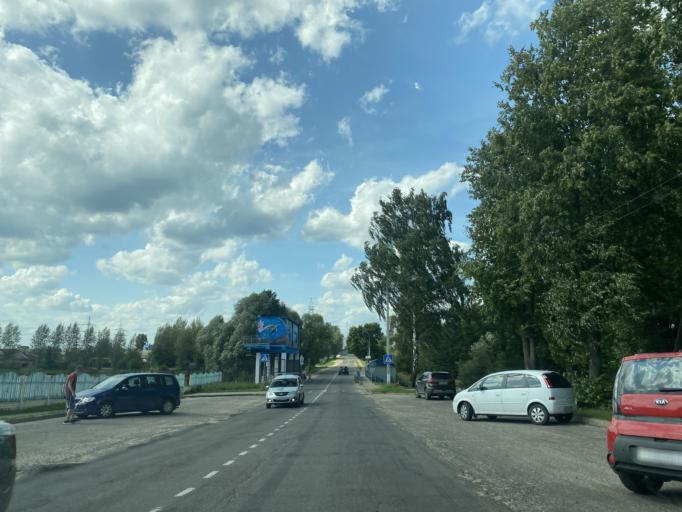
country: BY
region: Minsk
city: Horad Zhodzina
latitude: 54.0994
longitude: 28.3519
